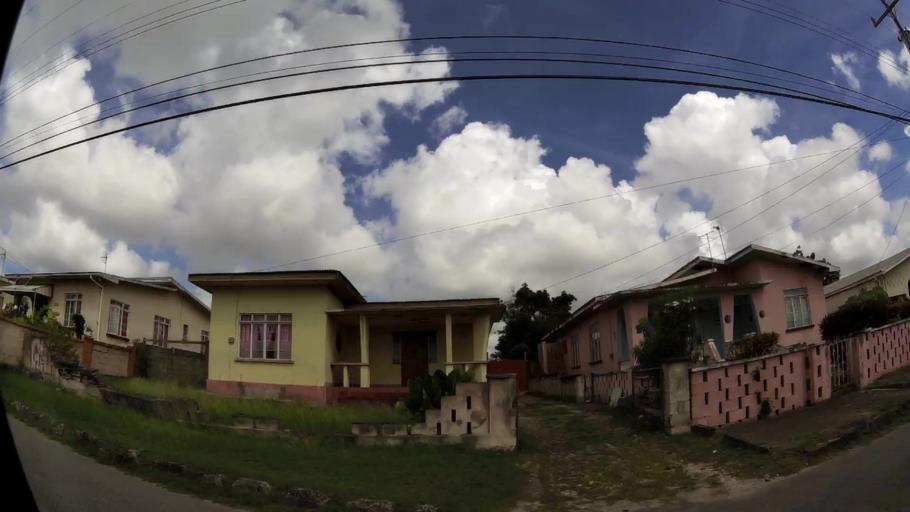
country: BB
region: Saint Michael
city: Bridgetown
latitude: 13.1273
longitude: -59.6163
